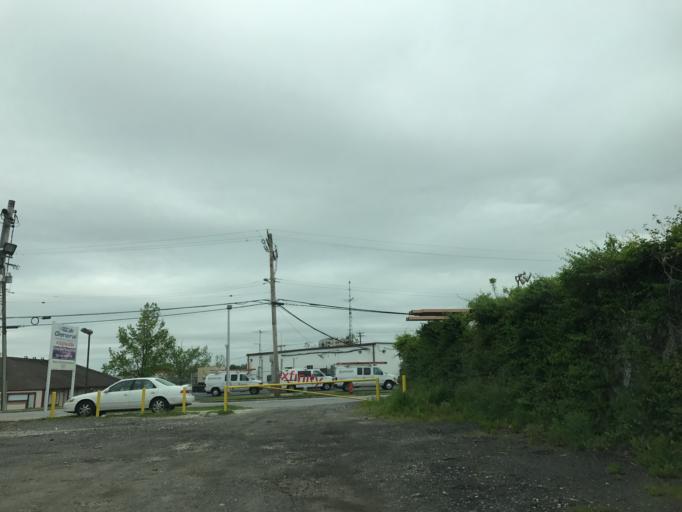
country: US
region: Maryland
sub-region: Baltimore County
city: Essex
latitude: 39.3157
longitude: -76.4590
